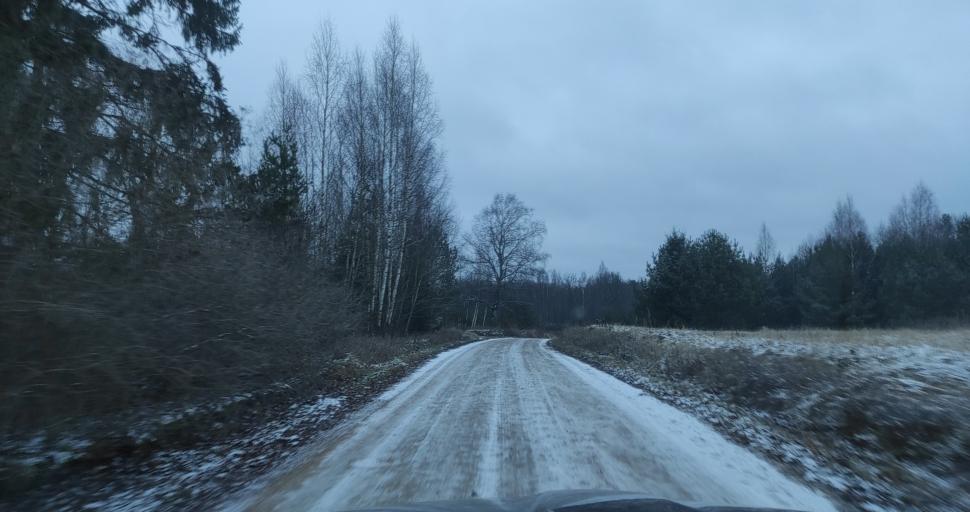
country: LV
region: Kuldigas Rajons
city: Kuldiga
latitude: 56.9793
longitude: 22.0520
